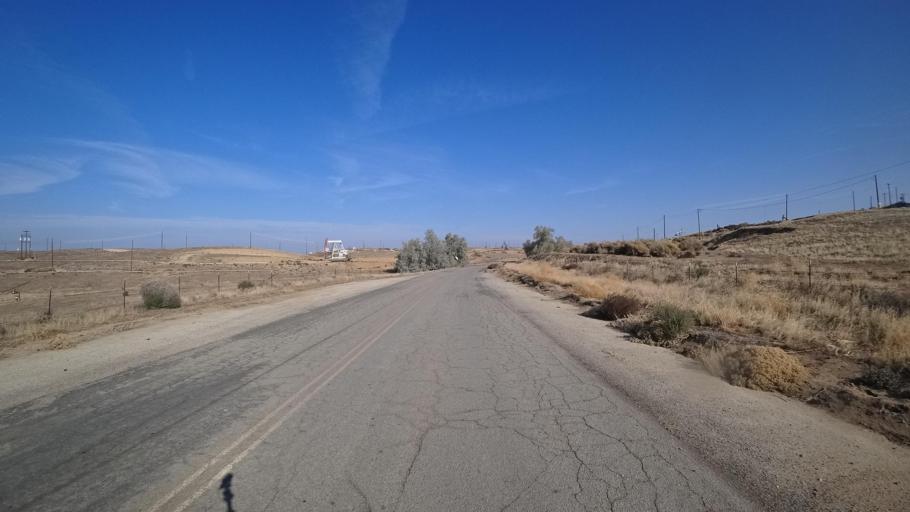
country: US
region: California
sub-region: Kern County
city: Oildale
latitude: 35.4959
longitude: -119.0400
